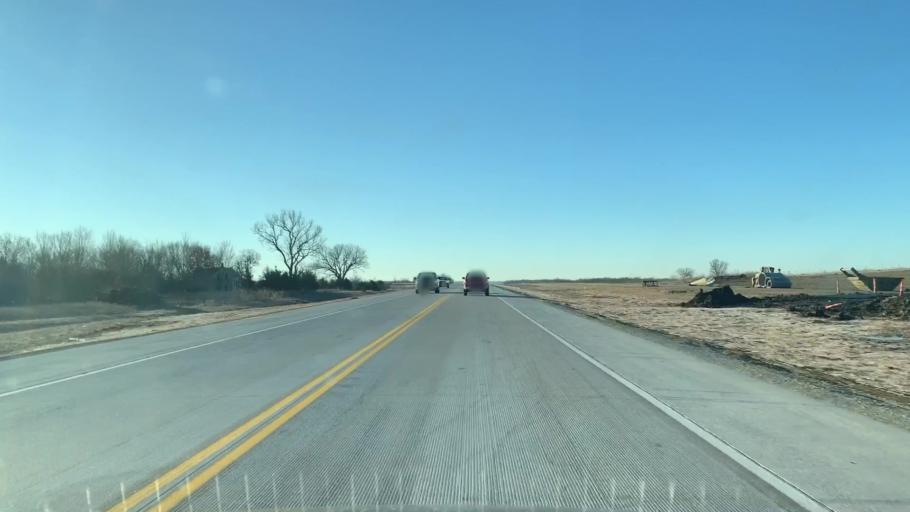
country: US
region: Kansas
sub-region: Bourbon County
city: Fort Scott
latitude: 37.7290
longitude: -94.7044
